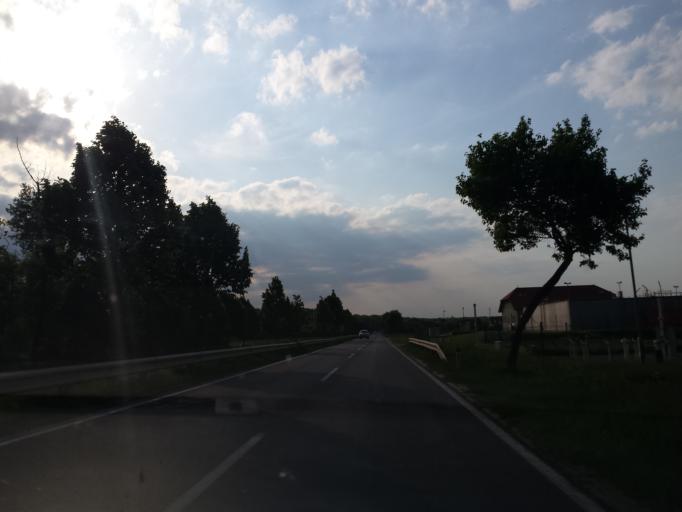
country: AT
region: Lower Austria
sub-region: Politischer Bezirk Ganserndorf
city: Untersiebenbrunn
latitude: 48.2642
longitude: 16.7241
